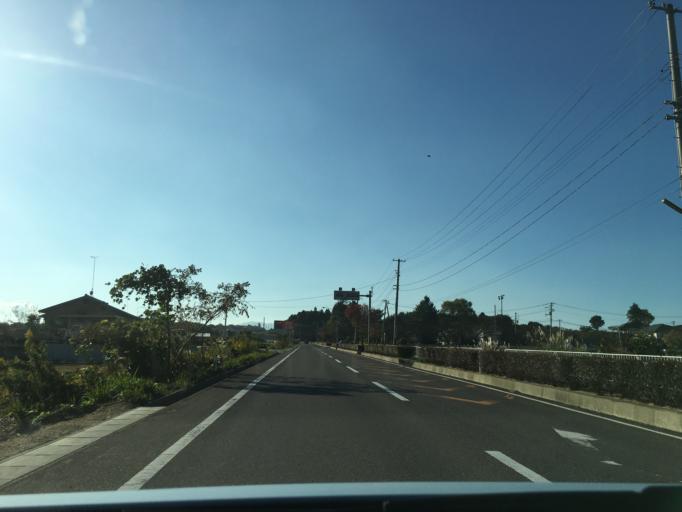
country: JP
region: Fukushima
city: Sukagawa
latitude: 37.3293
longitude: 140.3727
